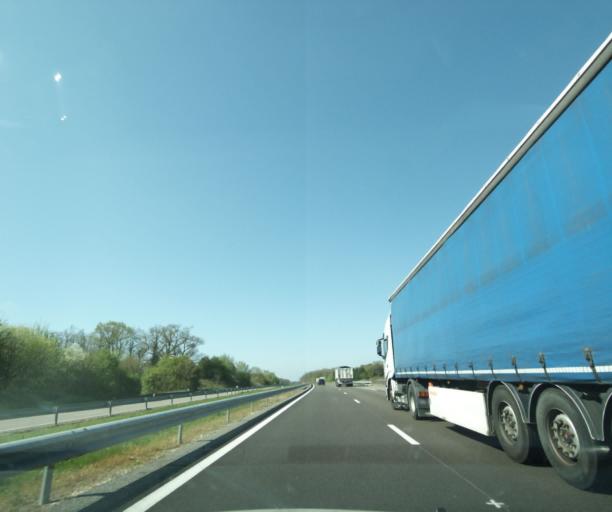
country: FR
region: Bourgogne
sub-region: Departement de la Nievre
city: Neuvy-sur-Loire
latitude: 47.4906
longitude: 2.9370
